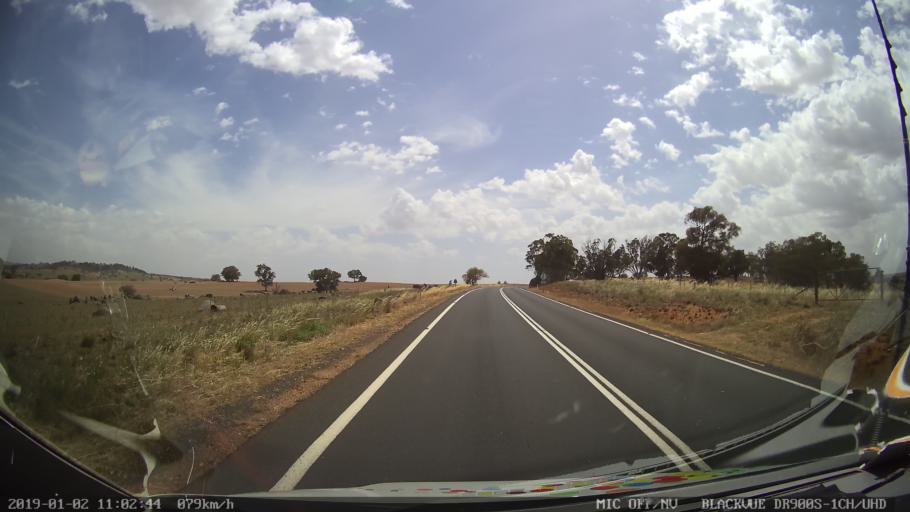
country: AU
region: New South Wales
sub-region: Young
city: Young
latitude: -34.5830
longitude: 148.3294
